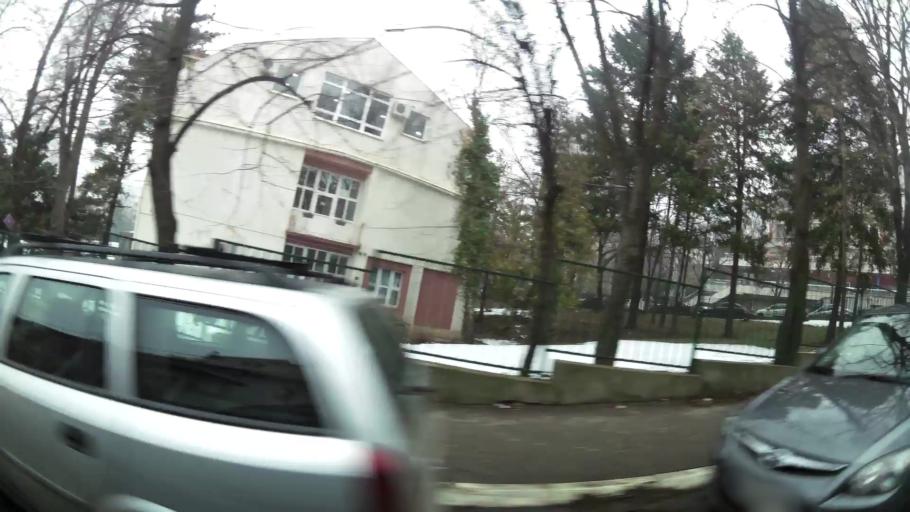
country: RS
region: Central Serbia
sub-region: Belgrade
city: Cukarica
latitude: 44.7778
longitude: 20.4160
